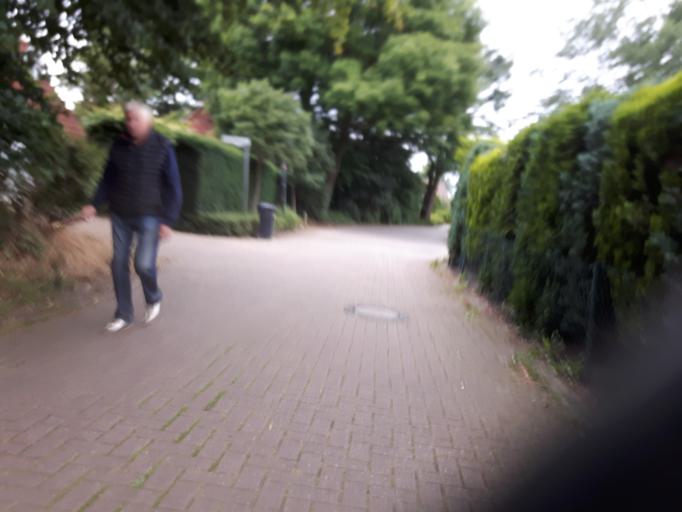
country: DE
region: Lower Saxony
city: Stuhr
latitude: 53.0291
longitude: 8.7352
